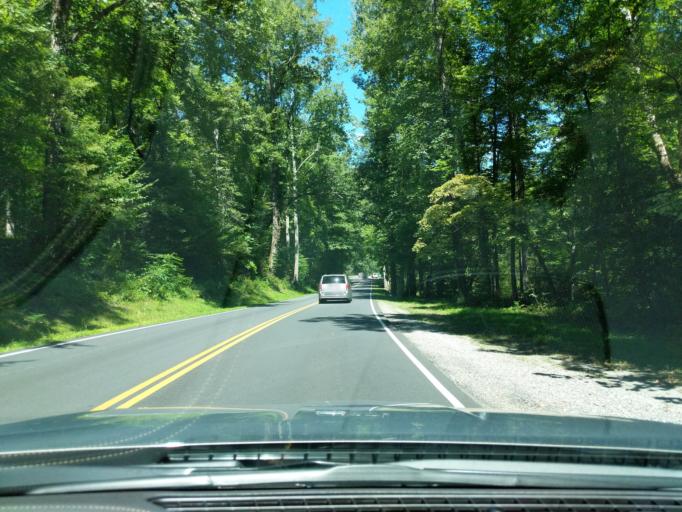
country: US
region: North Carolina
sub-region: Swain County
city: Cherokee
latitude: 35.5226
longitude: -83.3075
